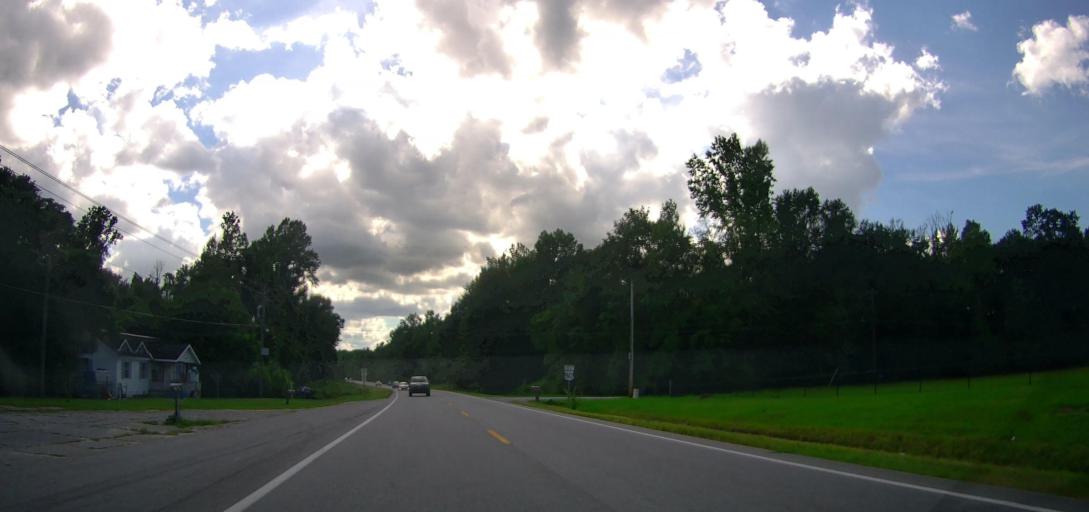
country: US
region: Alabama
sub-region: Russell County
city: Ladonia
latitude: 32.4622
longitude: -85.1670
